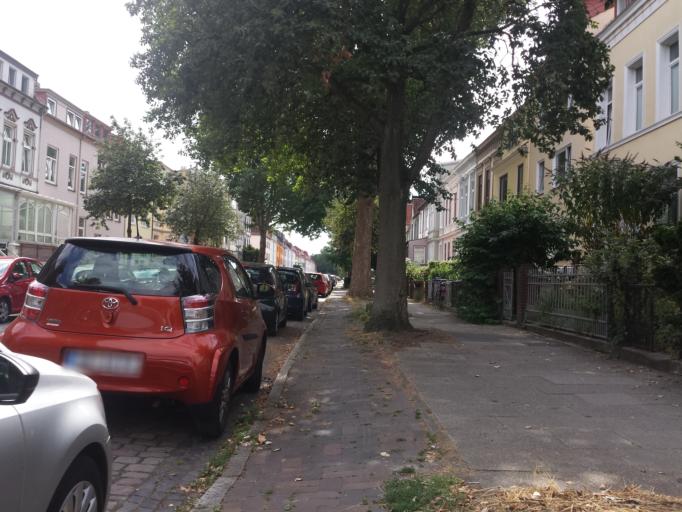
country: DE
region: Bremen
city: Bremen
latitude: 53.0641
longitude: 8.7960
